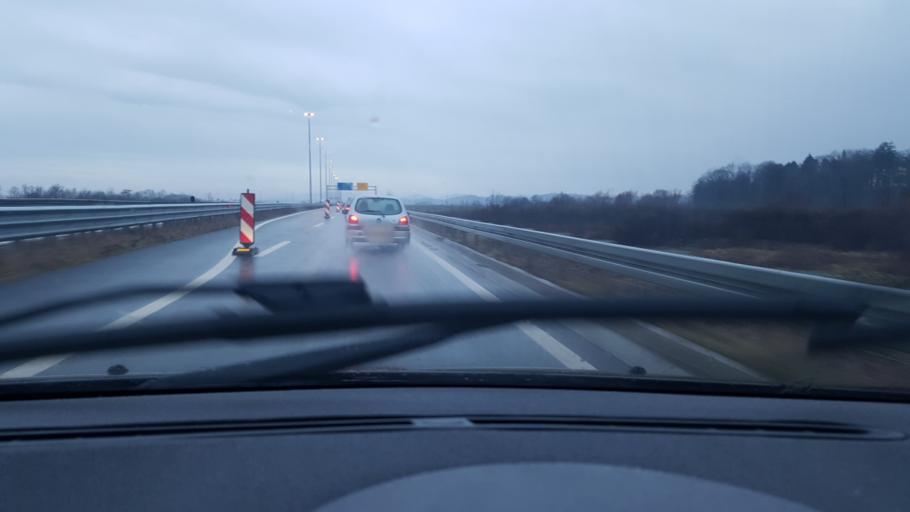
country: HR
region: Krapinsko-Zagorska
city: Zabok
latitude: 46.0134
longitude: 15.9431
